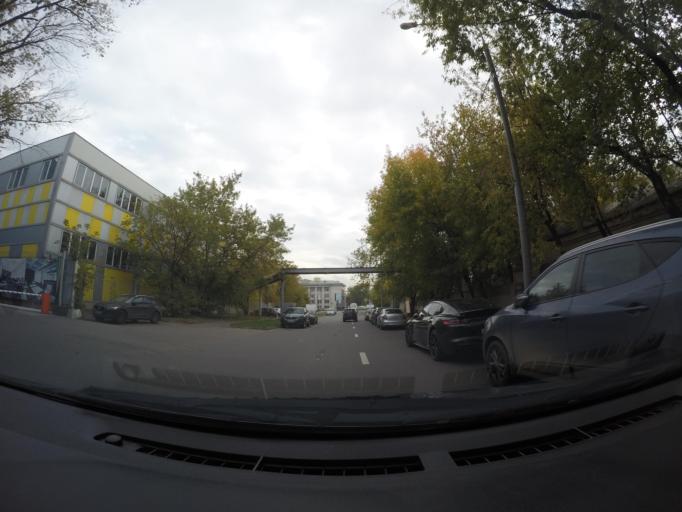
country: RU
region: Moscow
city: Lefortovo
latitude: 55.7567
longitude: 37.7351
